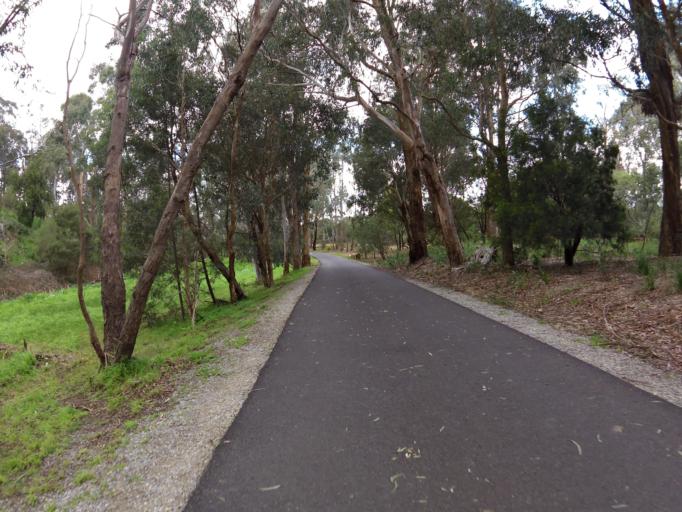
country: AU
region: Victoria
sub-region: Maroondah
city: Heathmont
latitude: -37.8398
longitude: 145.2358
